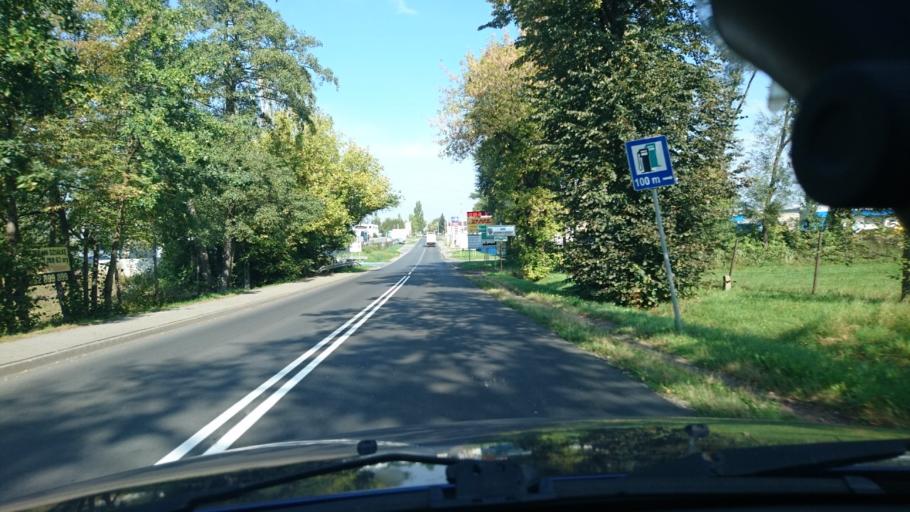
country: PL
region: Silesian Voivodeship
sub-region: Powiat bielski
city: Bestwina
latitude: 49.8680
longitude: 19.0297
